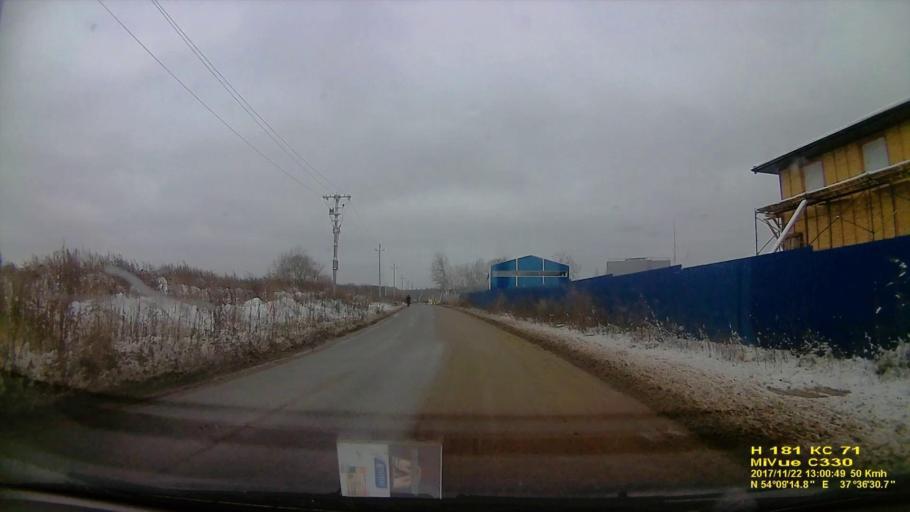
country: RU
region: Tula
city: Mendeleyevskiy
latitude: 54.1541
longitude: 37.6085
